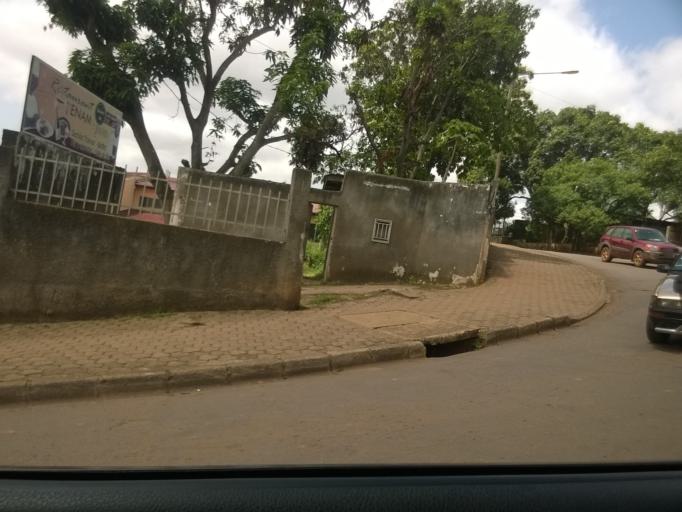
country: CM
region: Centre
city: Yaounde
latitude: 3.8622
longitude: 11.5099
